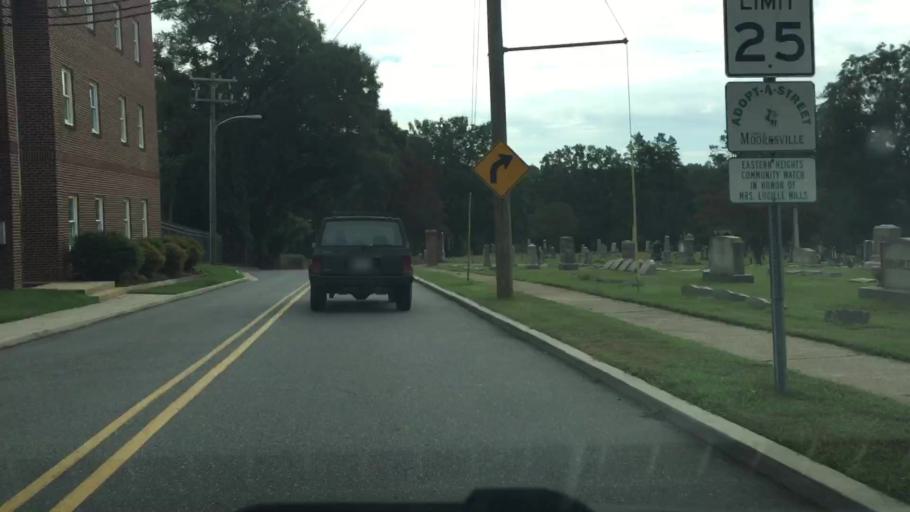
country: US
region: North Carolina
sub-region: Iredell County
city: Mooresville
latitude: 35.5805
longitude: -80.8123
